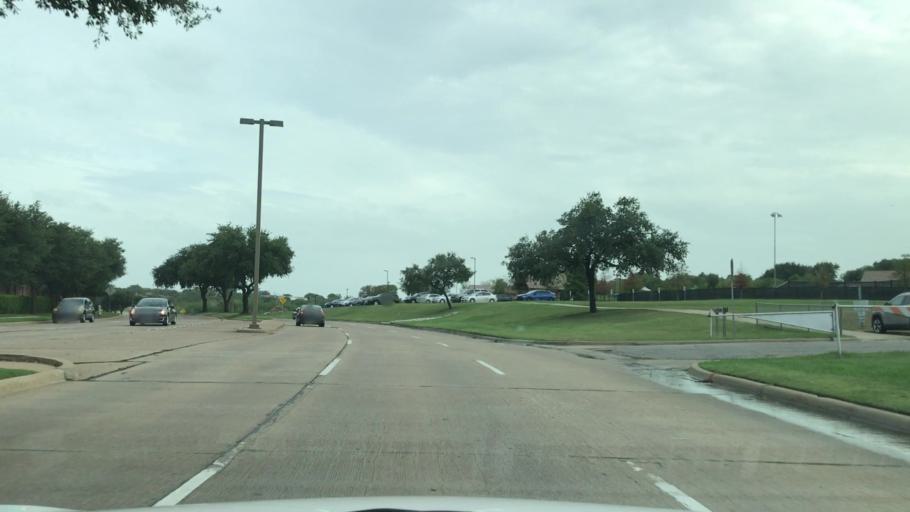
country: US
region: Texas
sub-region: Dallas County
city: Irving
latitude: 32.8634
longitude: -96.9773
